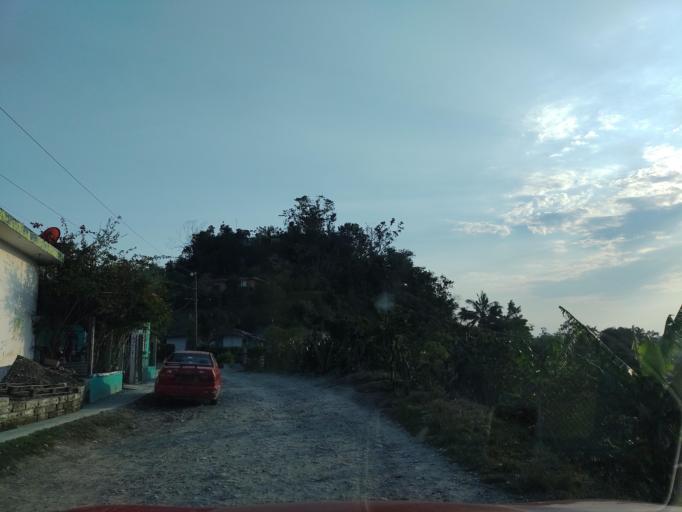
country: MX
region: Veracruz
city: Agua Dulce
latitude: 20.4042
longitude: -97.2892
